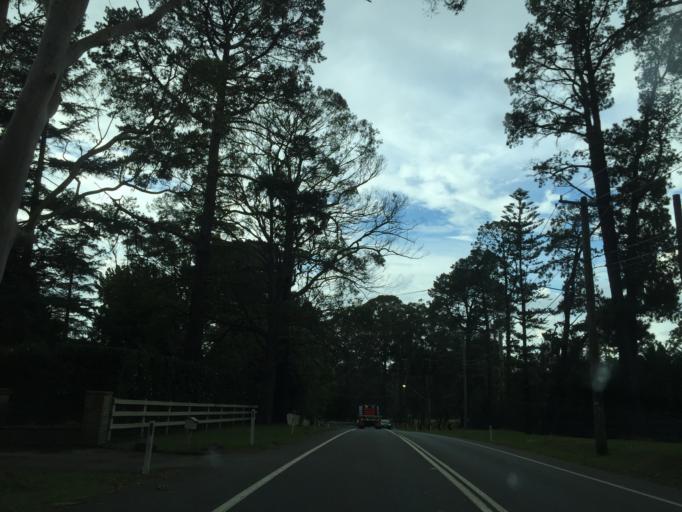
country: AU
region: New South Wales
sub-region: Hornsby Shire
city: Galston
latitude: -33.6705
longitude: 151.0367
